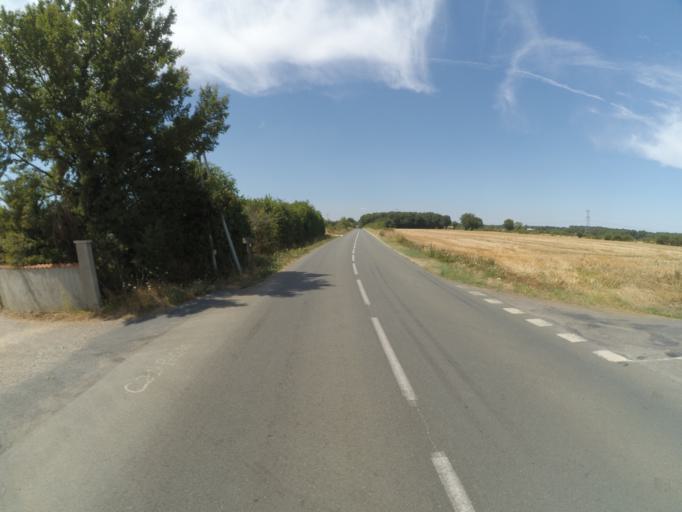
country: FR
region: Poitou-Charentes
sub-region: Departement de la Vienne
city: Saint-Maurice-la-Clouere
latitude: 46.3909
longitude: 0.3876
